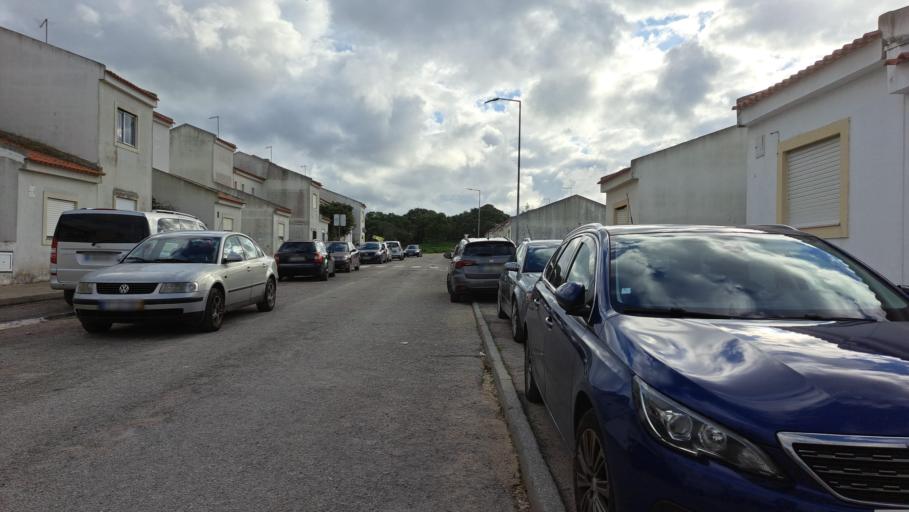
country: PT
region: Setubal
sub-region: Moita
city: Alhos Vedros
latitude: 38.6447
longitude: -9.0344
